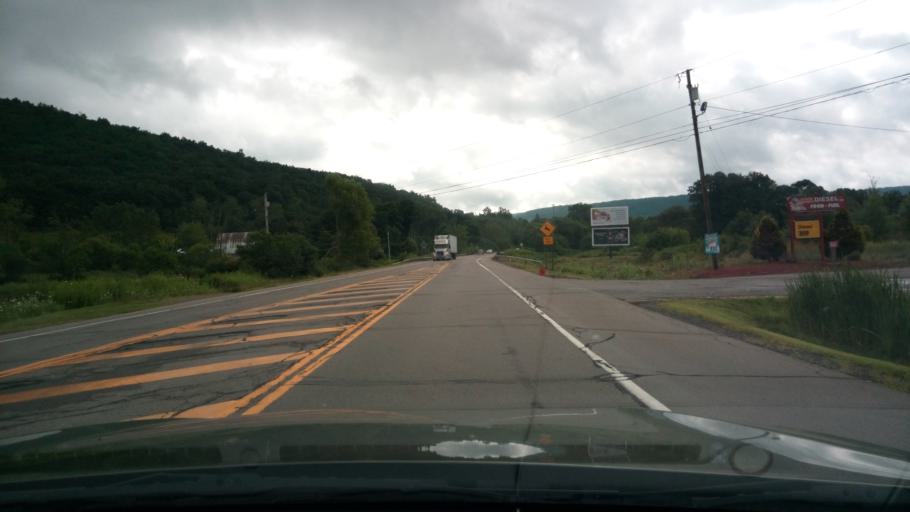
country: US
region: New York
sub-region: Chemung County
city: Horseheads North
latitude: 42.2937
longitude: -76.7142
